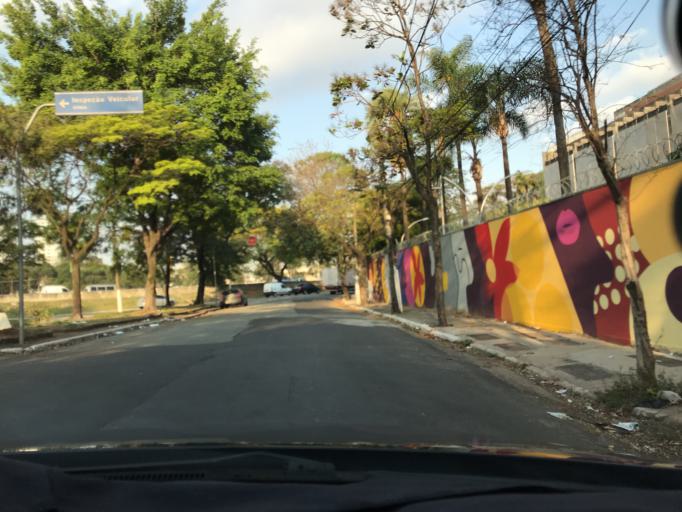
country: BR
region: Sao Paulo
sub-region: Osasco
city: Osasco
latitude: -23.5337
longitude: -46.7502
